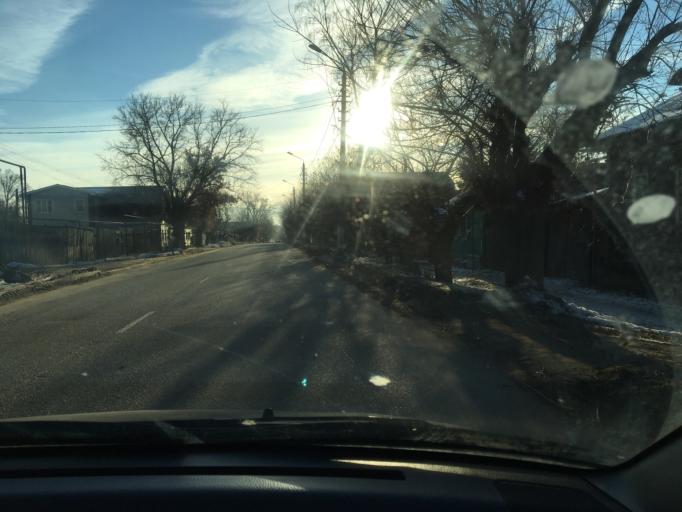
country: RU
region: Tula
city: Tula
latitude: 54.2191
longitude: 37.5975
